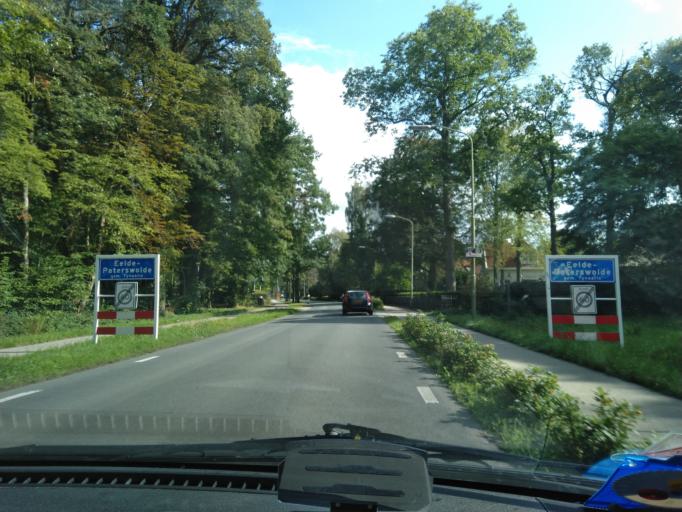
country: NL
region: Groningen
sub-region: Gemeente Haren
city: Haren
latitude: 53.1620
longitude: 6.5573
